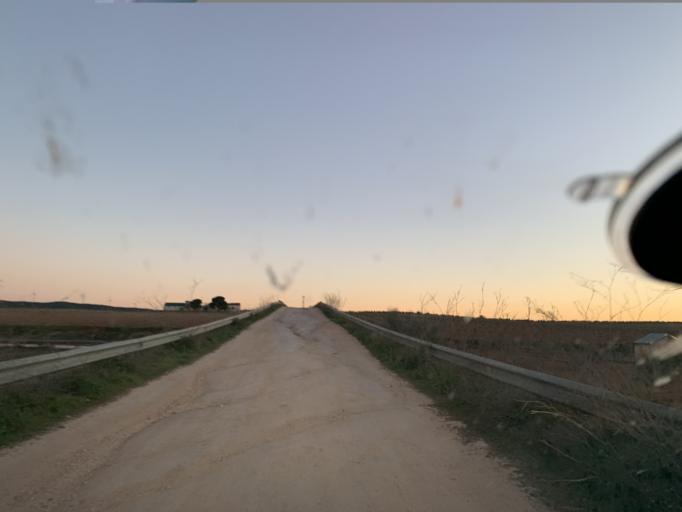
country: ES
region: Andalusia
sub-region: Provincia de Sevilla
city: Pedrera
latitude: 37.2140
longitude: -4.8508
